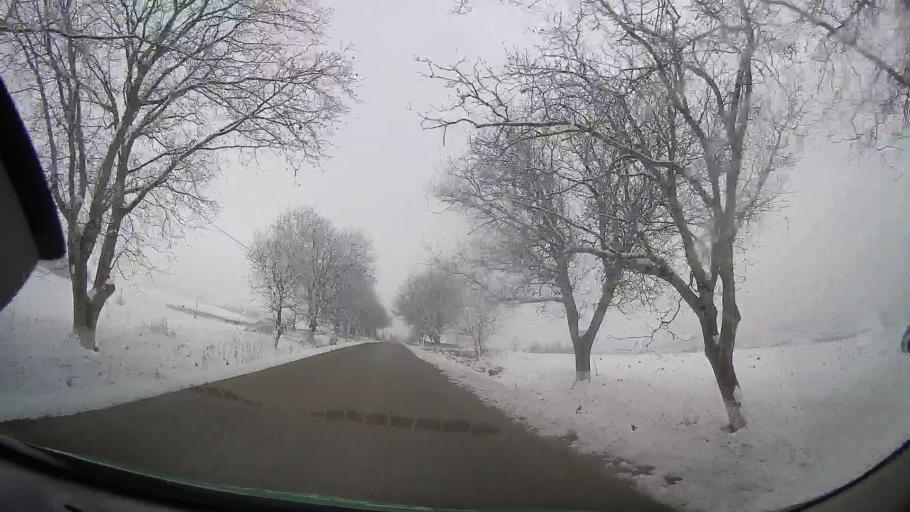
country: RO
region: Bacau
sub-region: Comuna Oncesti
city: Oncesti
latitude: 46.4462
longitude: 27.2645
